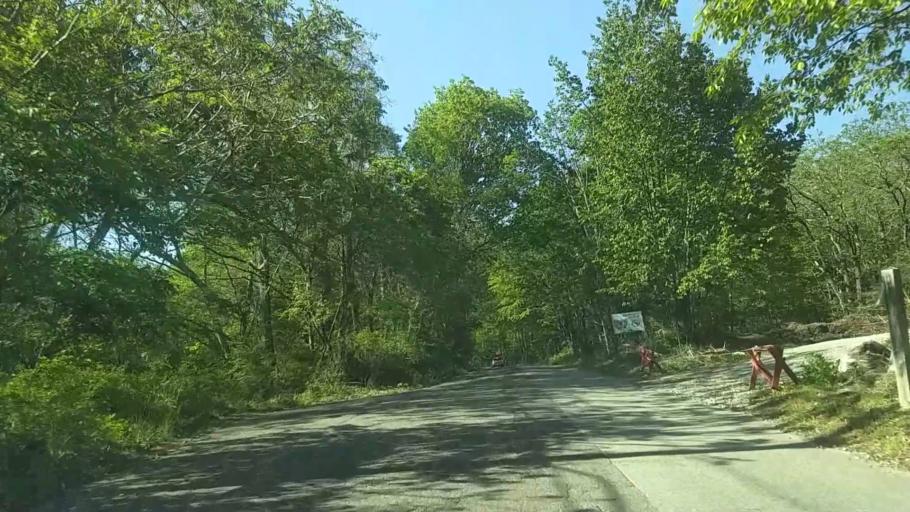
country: JP
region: Yamanashi
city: Nirasaki
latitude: 35.8877
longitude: 138.3564
